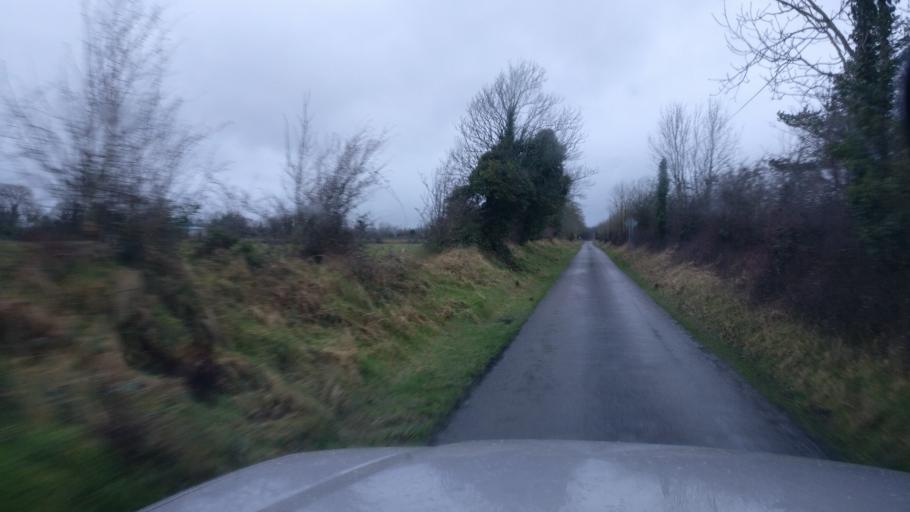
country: IE
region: Connaught
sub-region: County Galway
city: Ballinasloe
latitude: 53.2758
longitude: -8.3359
